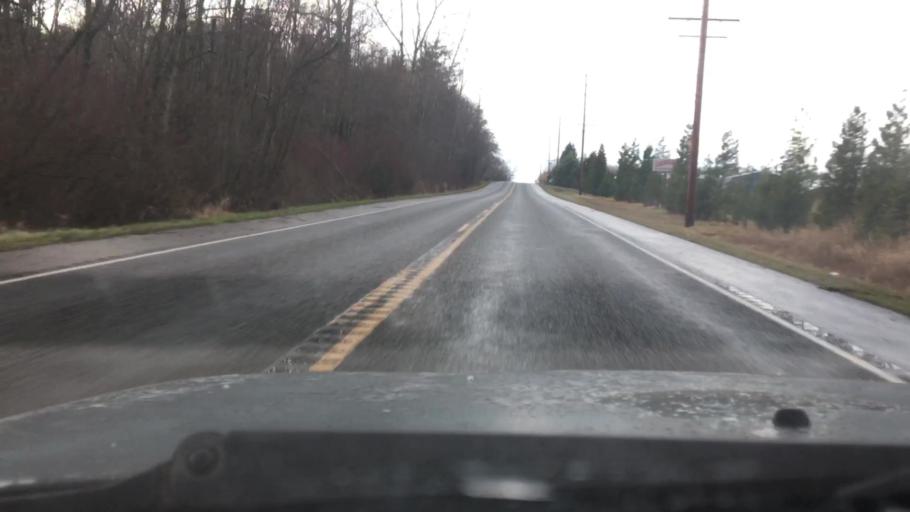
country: US
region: Washington
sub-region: Whatcom County
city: Ferndale
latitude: 48.8195
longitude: -122.6771
